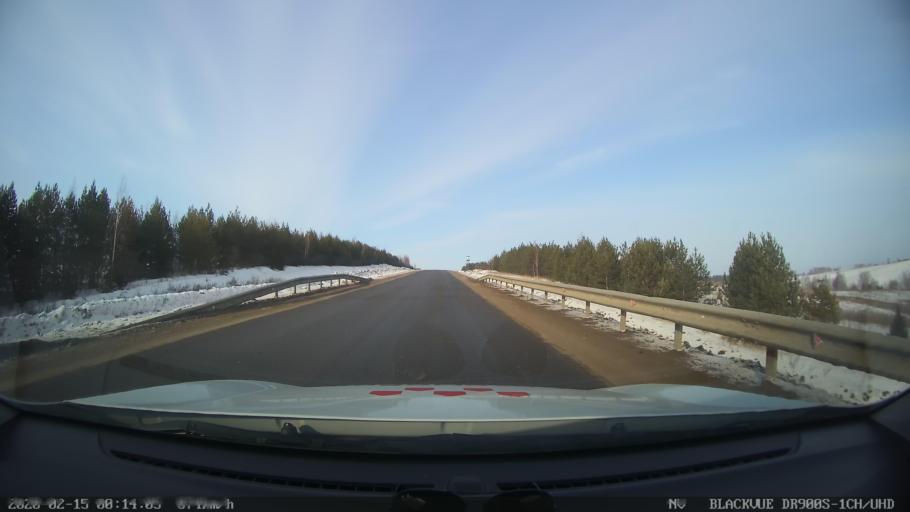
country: RU
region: Tatarstan
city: Stolbishchi
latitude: 55.4821
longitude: 49.0044
